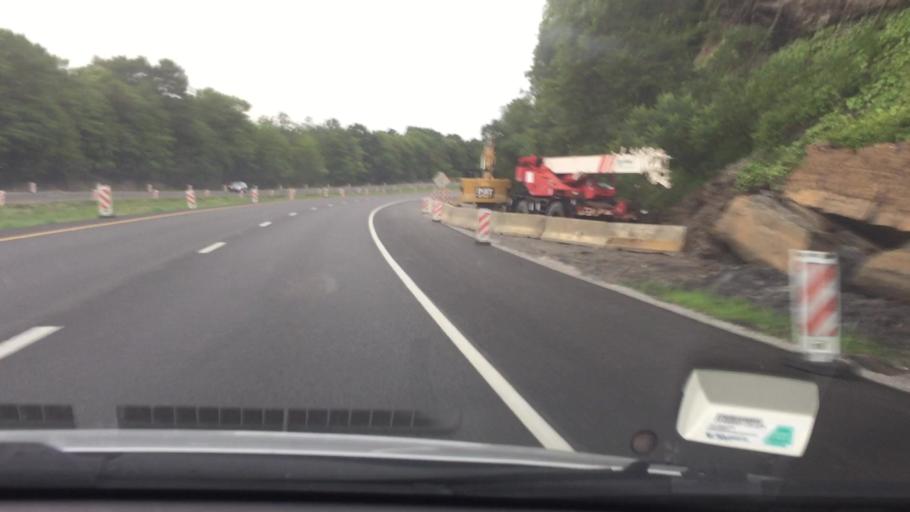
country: US
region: Pennsylvania
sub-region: Allegheny County
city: Brackenridge
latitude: 40.6458
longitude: -79.7207
